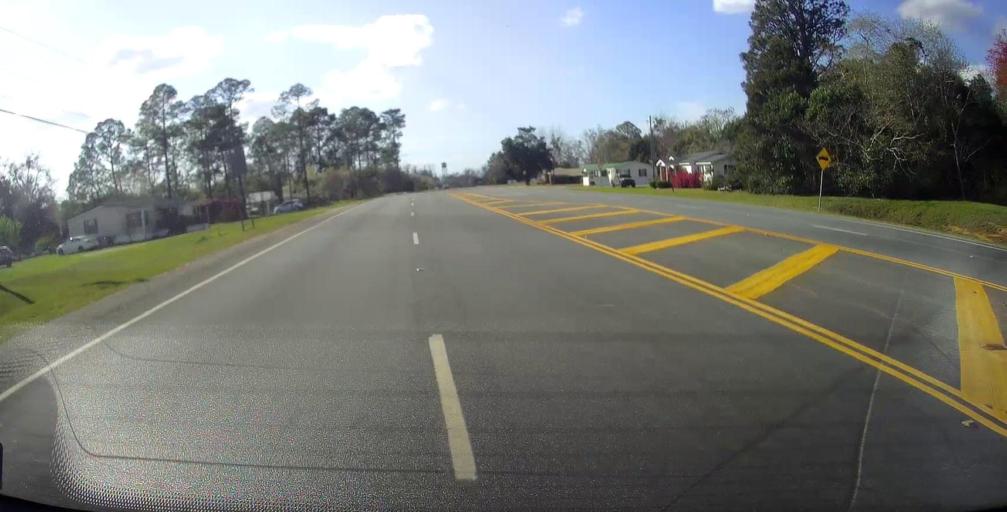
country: US
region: Georgia
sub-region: Telfair County
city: Helena
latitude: 32.1023
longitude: -83.0561
